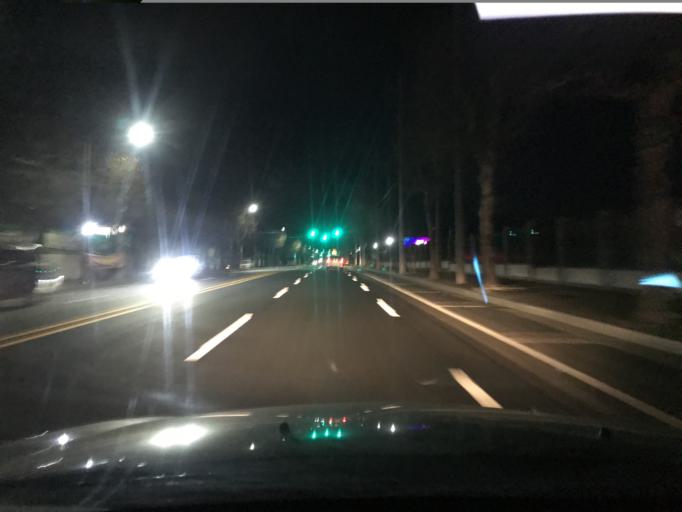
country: KR
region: Daegu
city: Hwawon
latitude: 35.7285
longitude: 128.4598
